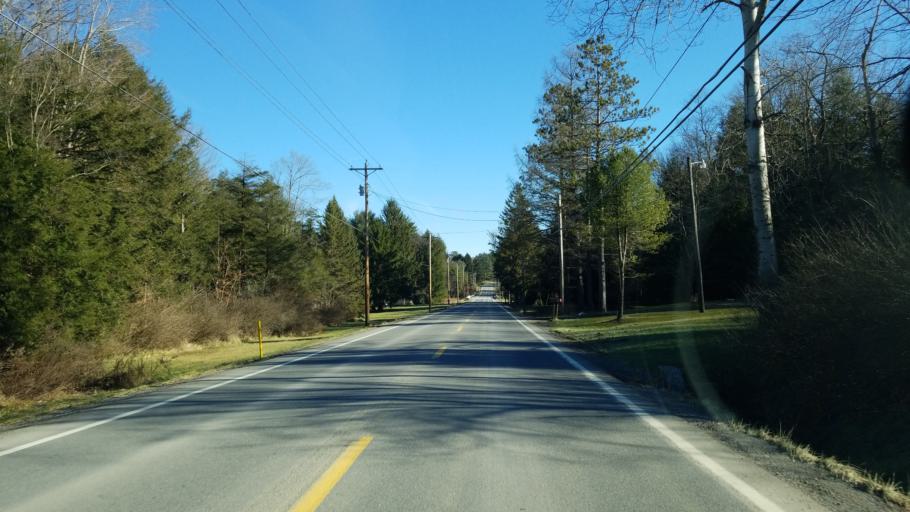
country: US
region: Pennsylvania
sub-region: Jefferson County
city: Falls Creek
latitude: 41.1772
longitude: -78.8488
